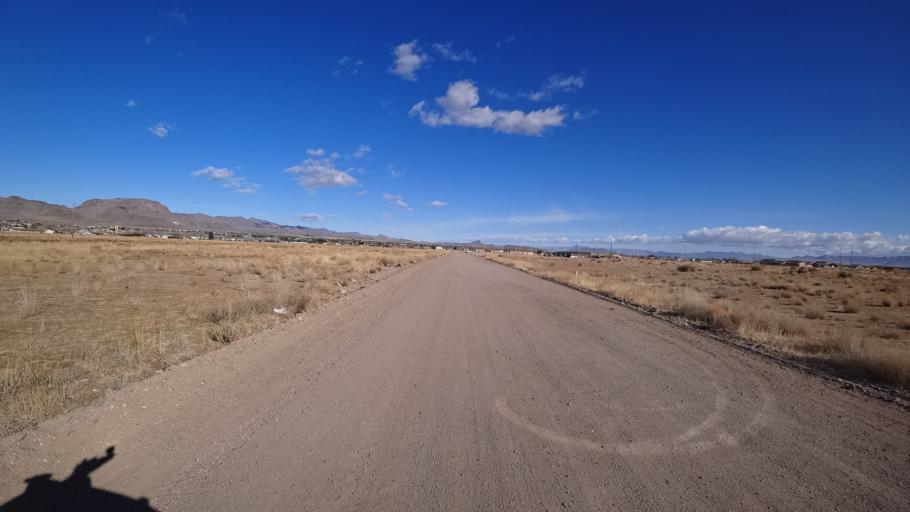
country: US
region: Arizona
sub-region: Mohave County
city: New Kingman-Butler
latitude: 35.2300
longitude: -114.0141
